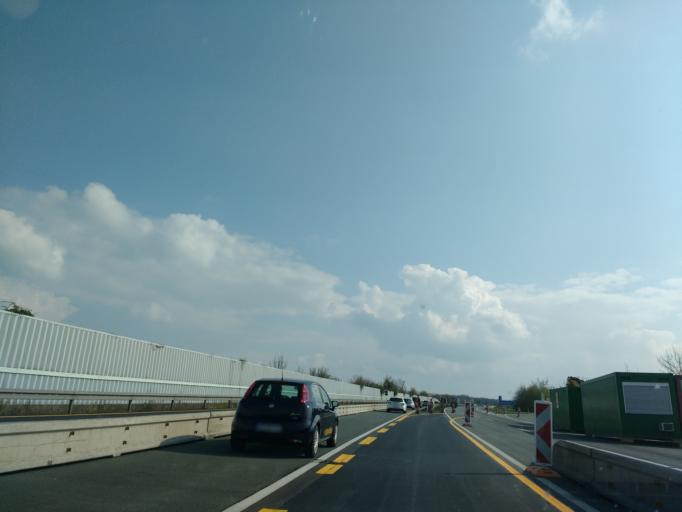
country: DE
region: North Rhine-Westphalia
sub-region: Regierungsbezirk Detmold
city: Paderborn
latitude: 51.6519
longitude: 8.7144
